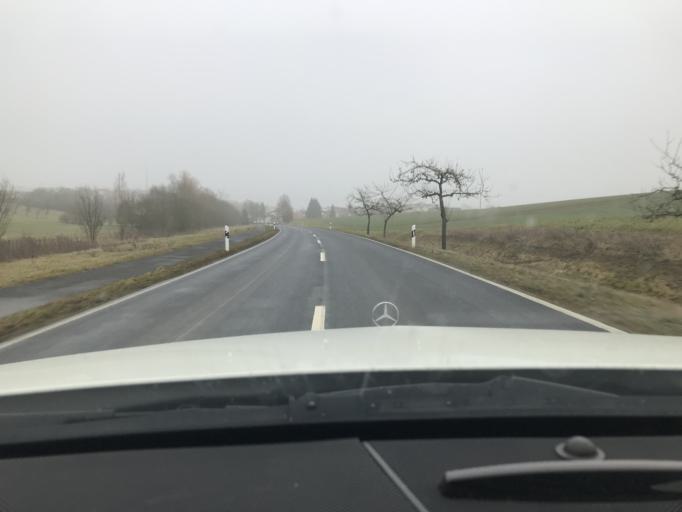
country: DE
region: Bavaria
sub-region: Regierungsbezirk Unterfranken
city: Werneck
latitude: 50.0063
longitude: 10.0605
